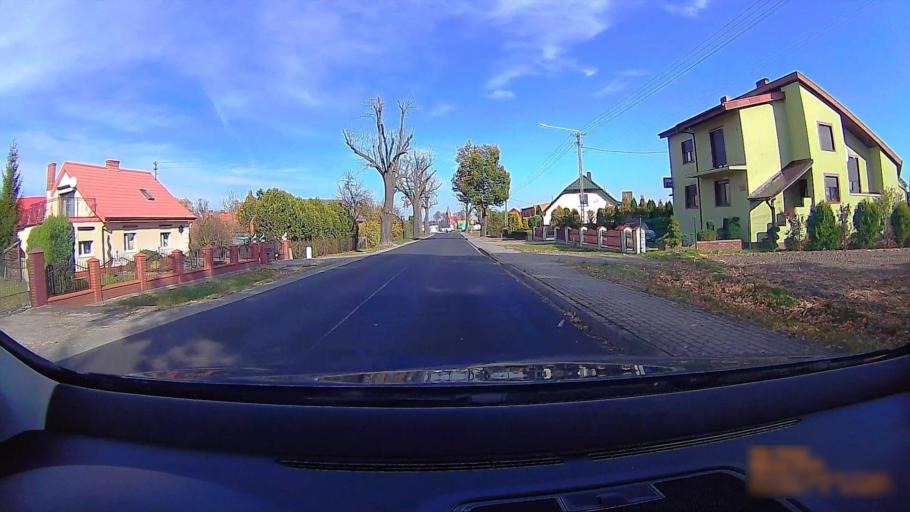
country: PL
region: Greater Poland Voivodeship
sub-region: Powiat ostrzeszowski
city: Doruchow
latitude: 51.4108
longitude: 18.0751
